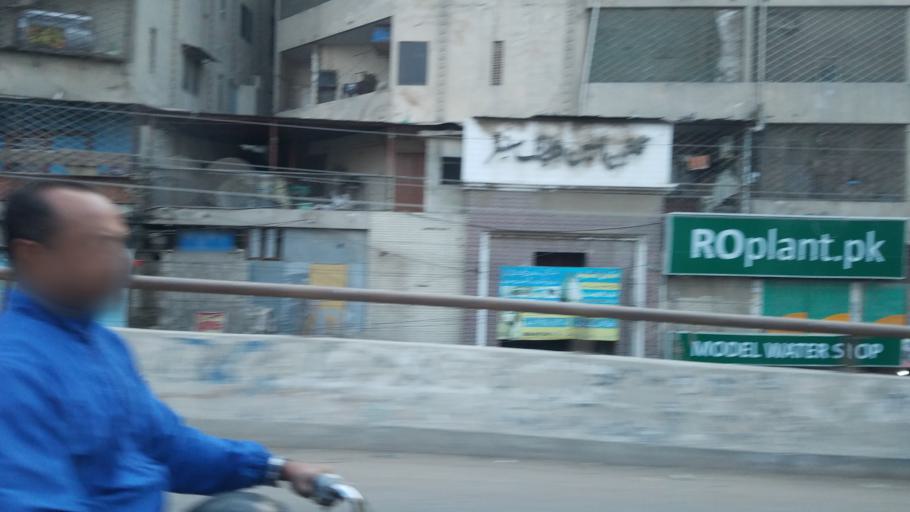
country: PK
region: Sindh
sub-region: Karachi District
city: Karachi
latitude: 24.9421
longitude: 67.0849
